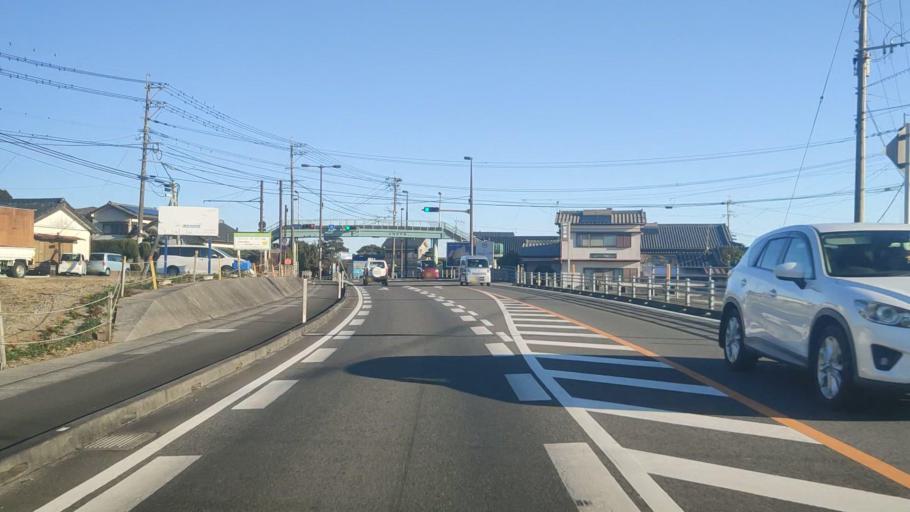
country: JP
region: Miyazaki
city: Nobeoka
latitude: 32.3719
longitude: 131.6305
